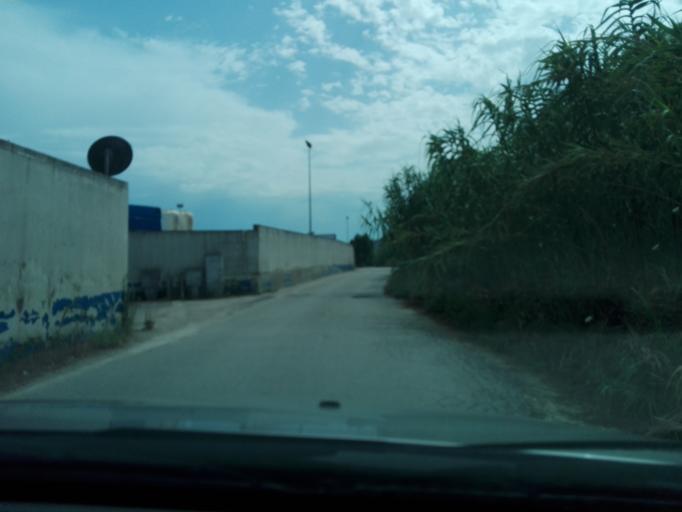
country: IT
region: Abruzzo
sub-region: Provincia di Pescara
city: Cappelle sul Tavo
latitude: 42.4881
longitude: 14.1119
